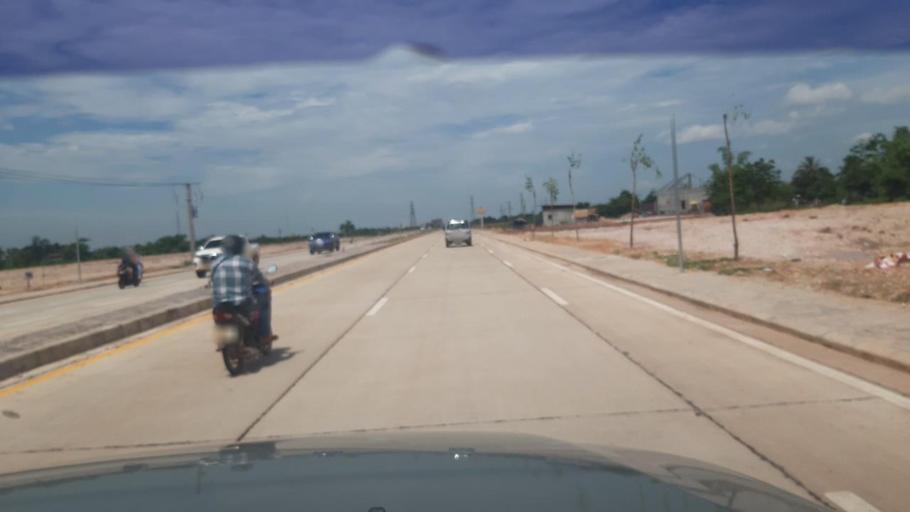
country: LA
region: Vientiane
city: Vientiane
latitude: 18.0276
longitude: 102.6049
